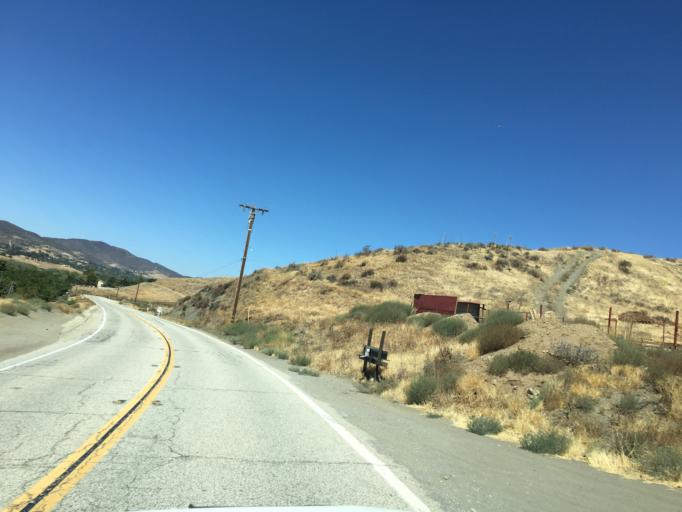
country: US
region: California
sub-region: Los Angeles County
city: Leona Valley
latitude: 34.6085
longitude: -118.2536
